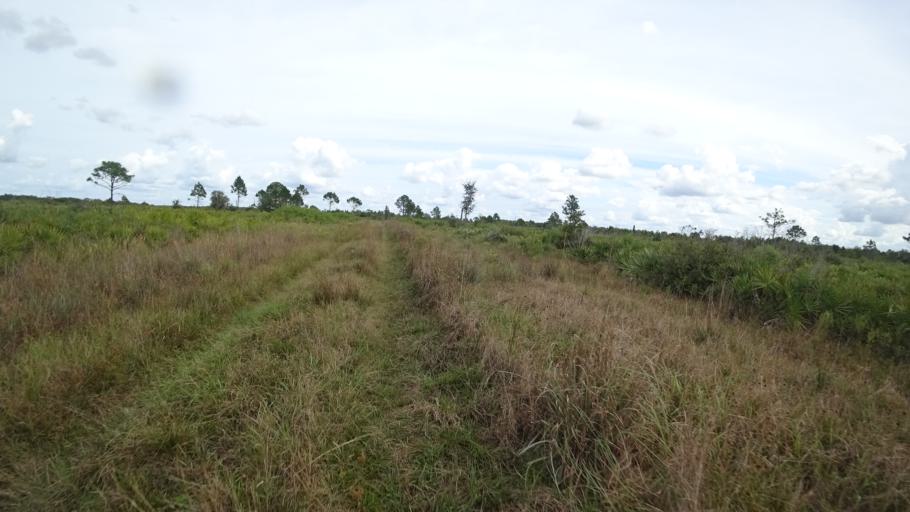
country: US
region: Florida
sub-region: Hillsborough County
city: Wimauma
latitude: 27.5589
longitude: -82.1278
